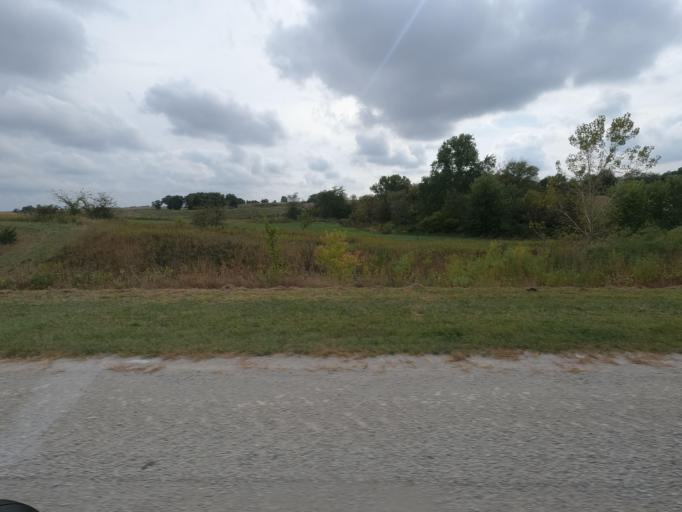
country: US
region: Iowa
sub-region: Wapello County
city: Ottumwa
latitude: 41.0022
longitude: -92.2753
